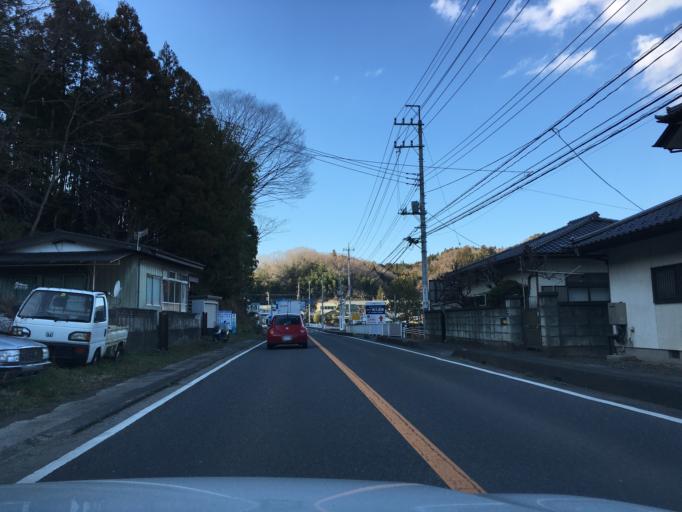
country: JP
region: Ibaraki
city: Daigo
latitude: 36.7560
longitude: 140.3828
